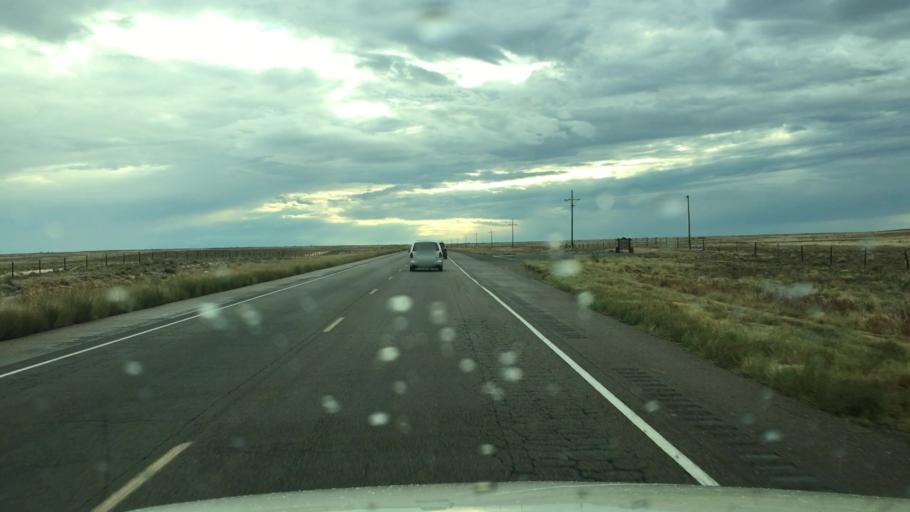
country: US
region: New Mexico
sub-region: Chaves County
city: Roswell
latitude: 33.4053
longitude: -104.3097
